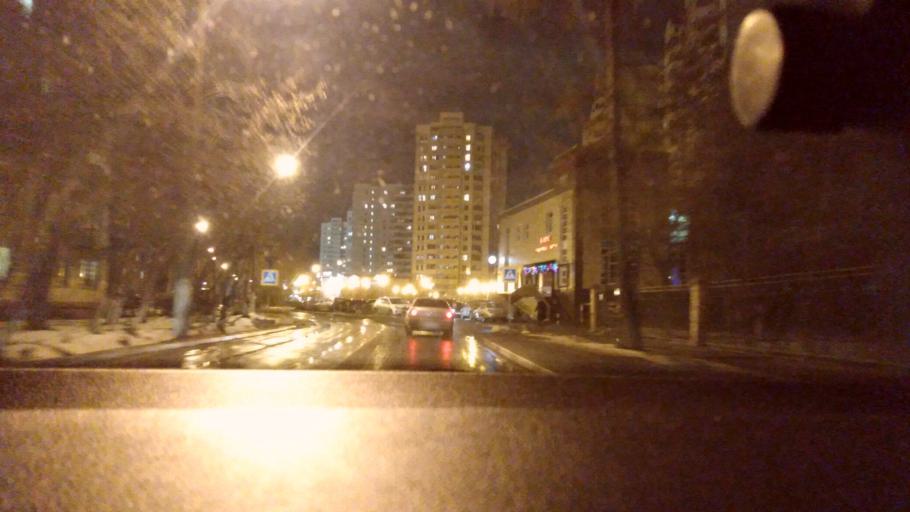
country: RU
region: Moskovskaya
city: Zheleznodorozhnyy
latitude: 55.7496
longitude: 37.9858
